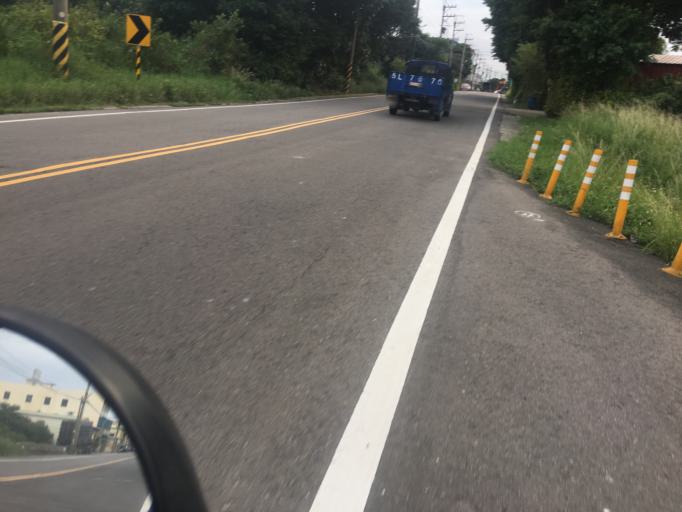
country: TW
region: Taiwan
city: Taoyuan City
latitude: 25.0969
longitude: 121.2361
